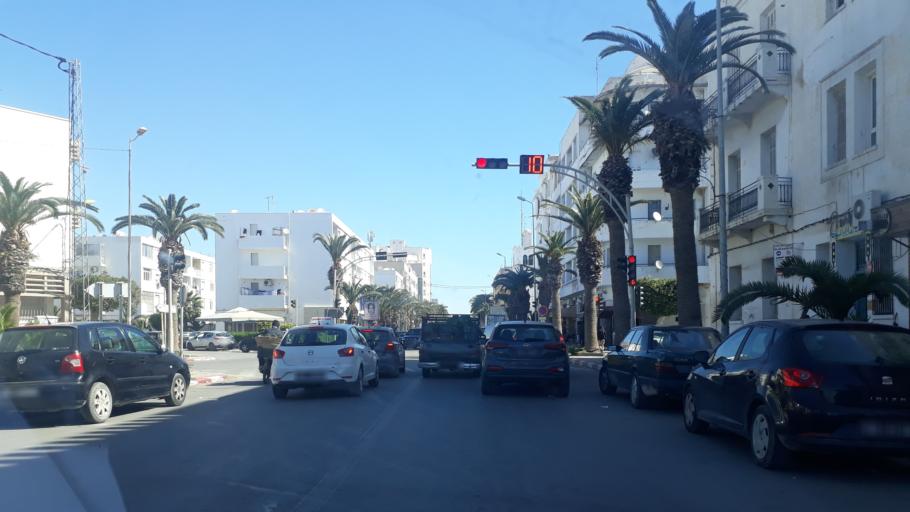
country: TN
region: Safaqis
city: Sfax
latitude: 34.7293
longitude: 10.7597
